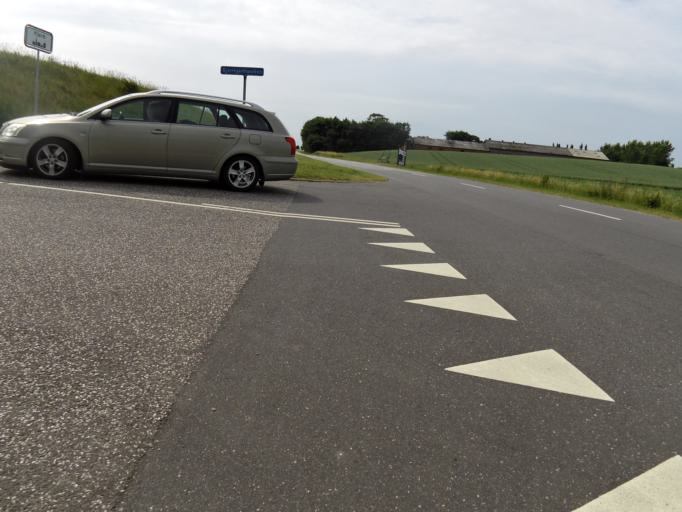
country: DK
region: Central Jutland
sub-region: Struer Kommune
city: Struer
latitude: 56.4355
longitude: 8.6285
